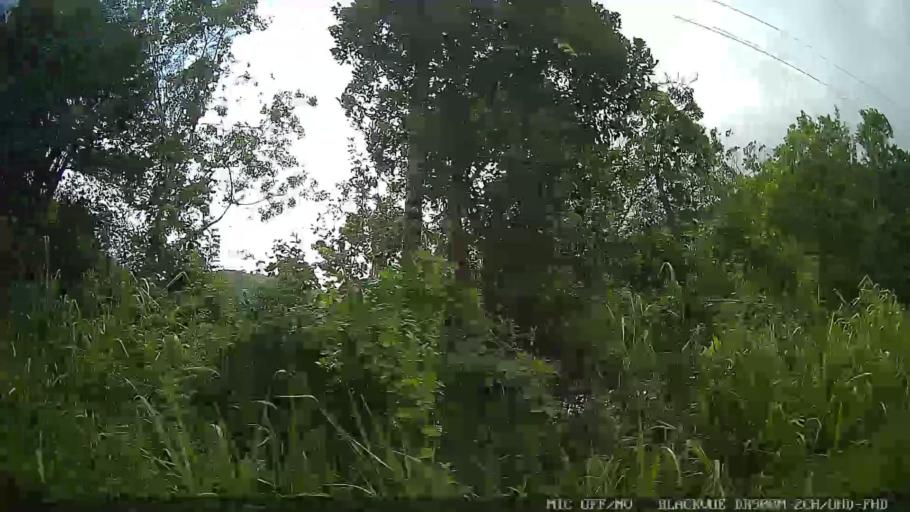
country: BR
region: Sao Paulo
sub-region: Caraguatatuba
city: Caraguatatuba
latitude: -23.6298
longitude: -45.4518
